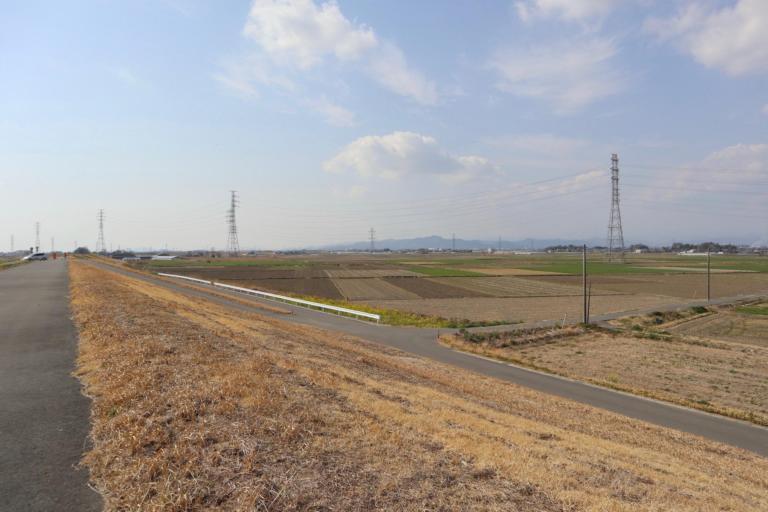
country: JP
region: Tochigi
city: Sano
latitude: 36.2702
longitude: 139.5969
